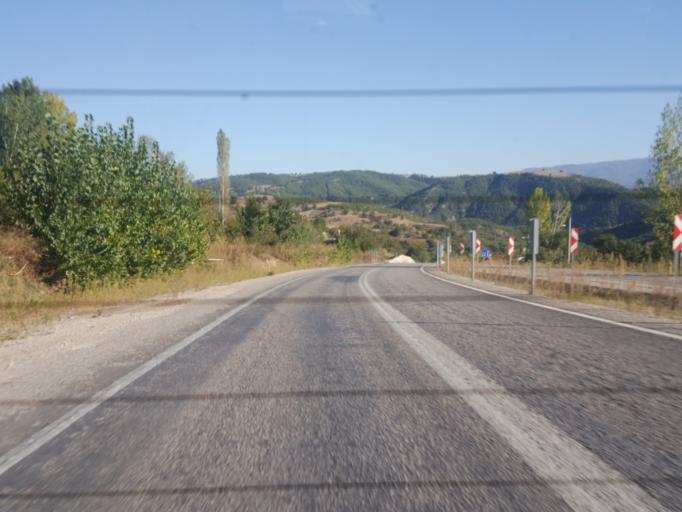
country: TR
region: Amasya
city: Tasova
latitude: 40.7631
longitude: 36.2815
